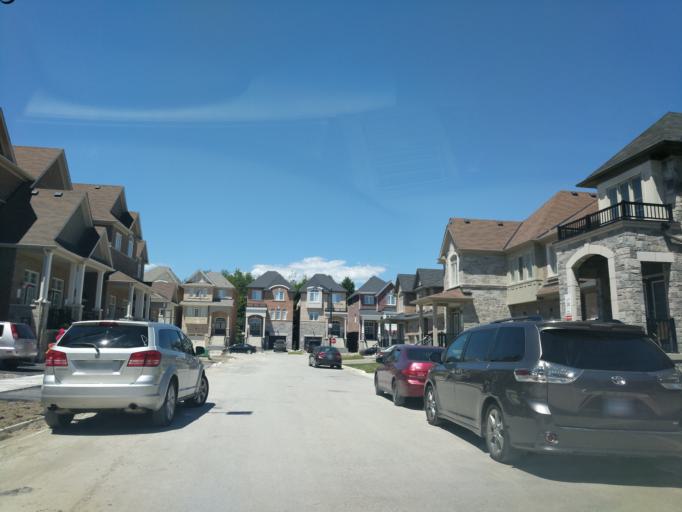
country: CA
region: Ontario
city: Ajax
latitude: 43.8548
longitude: -79.0749
